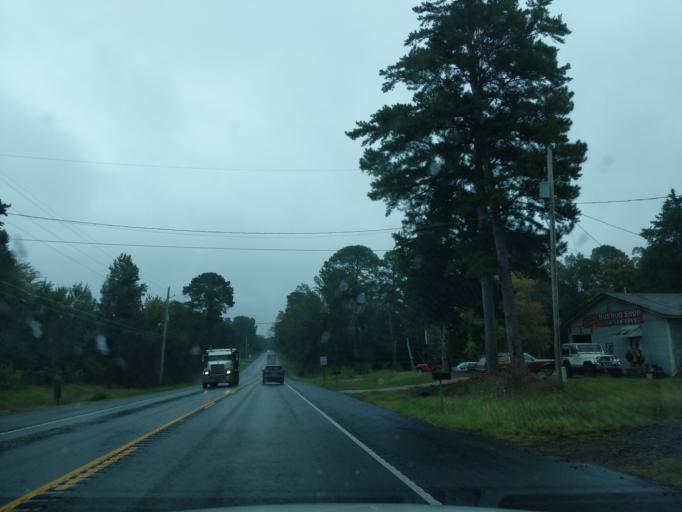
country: US
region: Louisiana
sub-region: Caddo Parish
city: Greenwood
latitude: 32.3756
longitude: -94.0327
